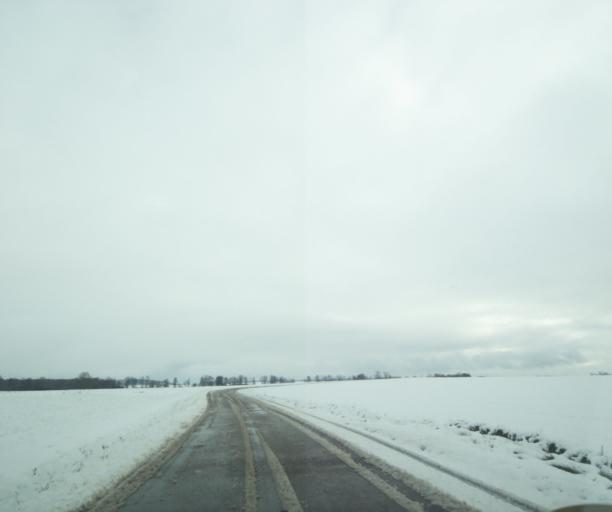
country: FR
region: Champagne-Ardenne
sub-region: Departement de la Haute-Marne
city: Montier-en-Der
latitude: 48.4487
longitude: 4.7002
